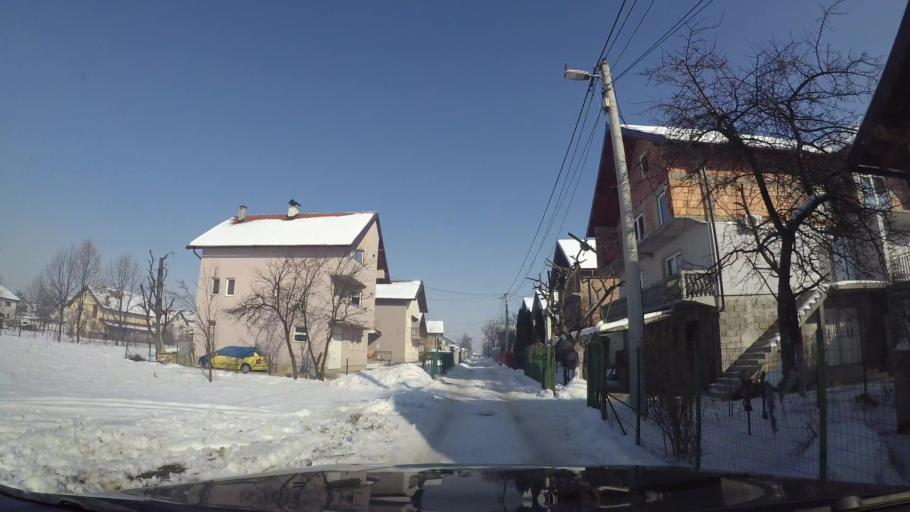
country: BA
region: Federation of Bosnia and Herzegovina
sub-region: Kanton Sarajevo
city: Sarajevo
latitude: 43.8009
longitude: 18.3066
